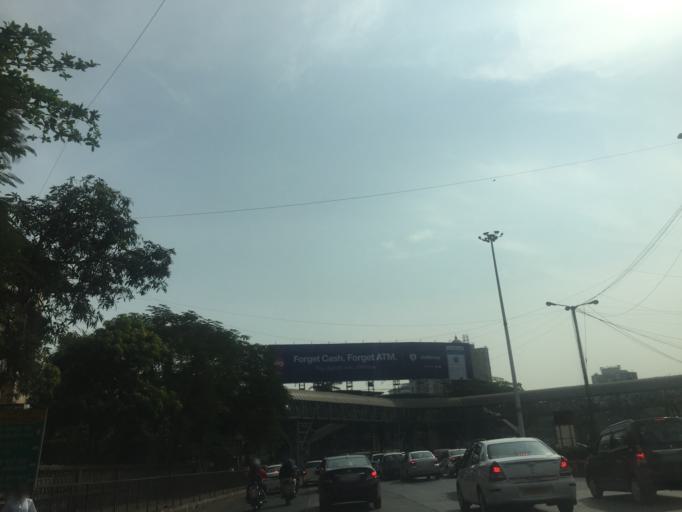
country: IN
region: Maharashtra
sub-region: Thane
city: Airoli
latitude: 19.1490
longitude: 72.9920
